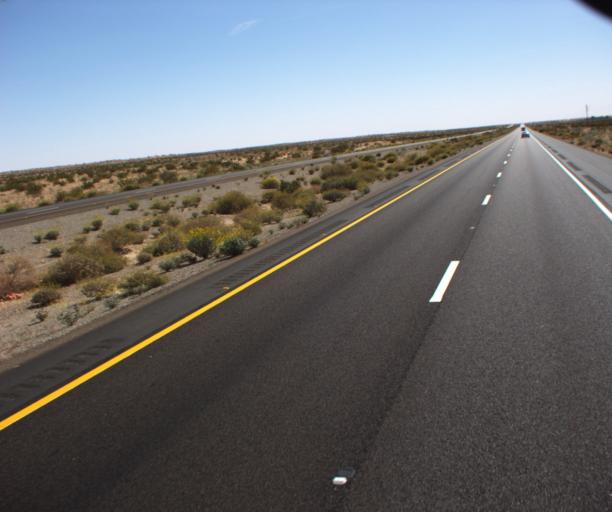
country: US
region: Arizona
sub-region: Yuma County
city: Somerton
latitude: 32.5818
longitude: -114.5522
